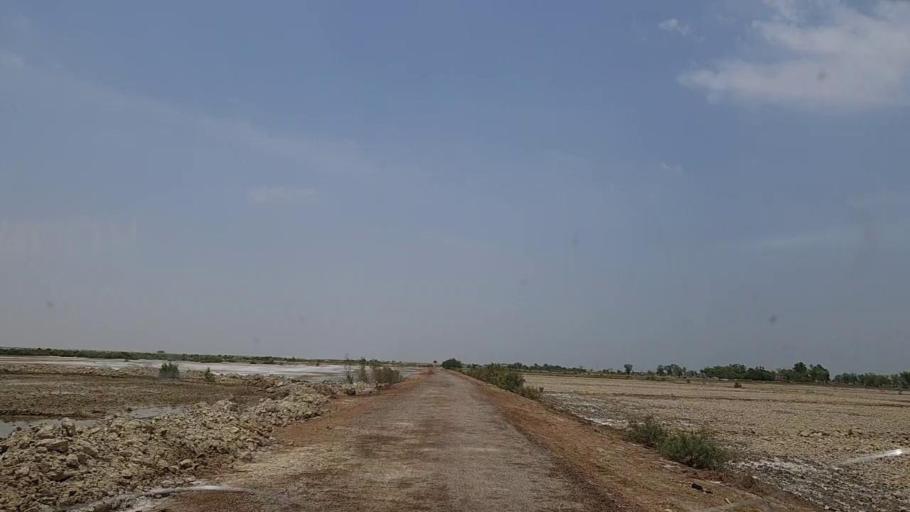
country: PK
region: Sindh
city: Phulji
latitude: 26.8671
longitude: 67.6531
